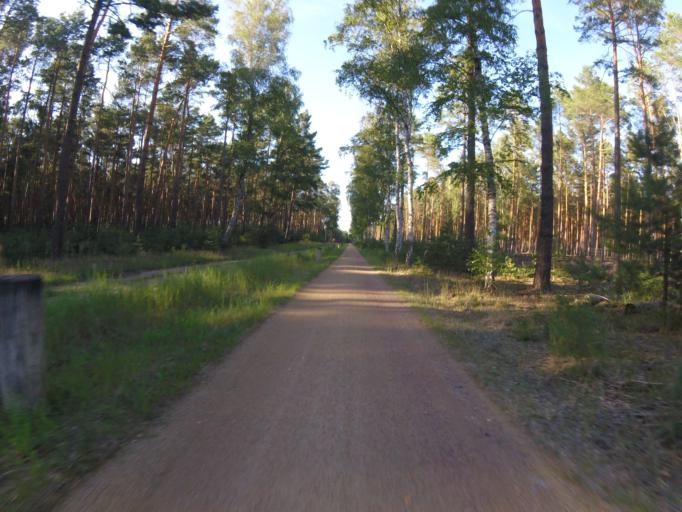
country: DE
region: Brandenburg
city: Halbe
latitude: 52.1917
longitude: 13.7619
